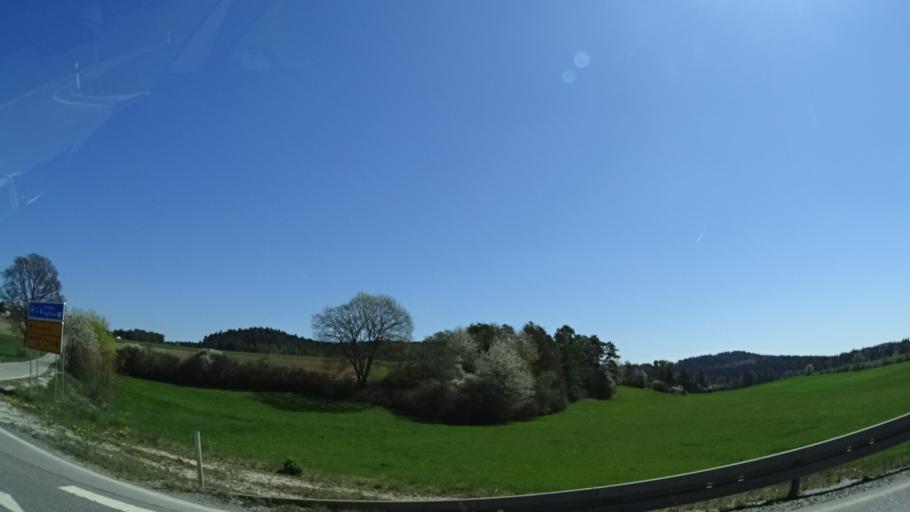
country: DE
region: Bavaria
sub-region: Upper Palatinate
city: Kastl
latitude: 49.3857
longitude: 11.7042
